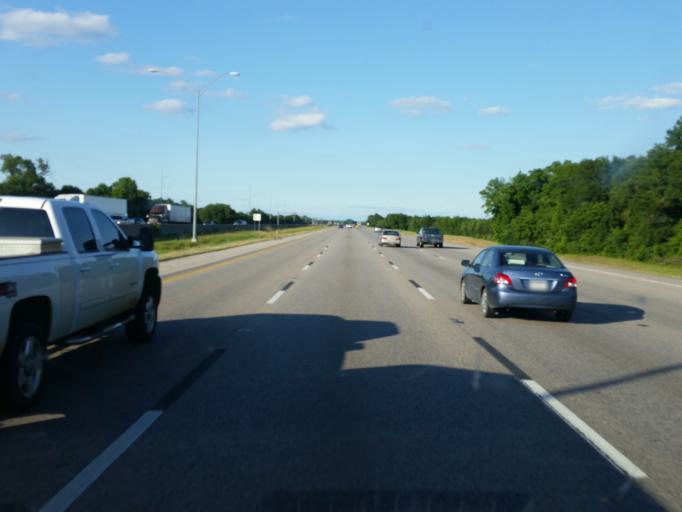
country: US
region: Texas
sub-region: Dallas County
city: Hutchins
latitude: 32.6669
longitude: -96.7159
